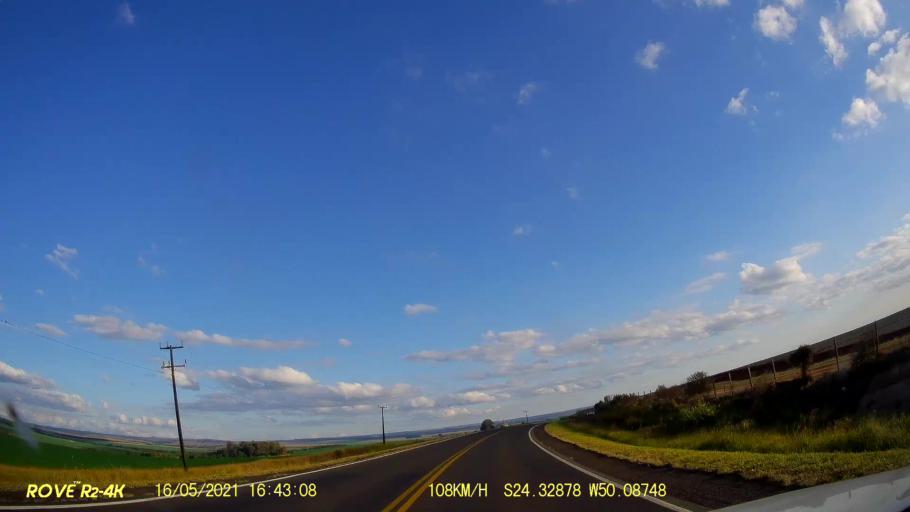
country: BR
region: Parana
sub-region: Pirai Do Sul
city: Pirai do Sul
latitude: -24.3292
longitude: -50.0875
